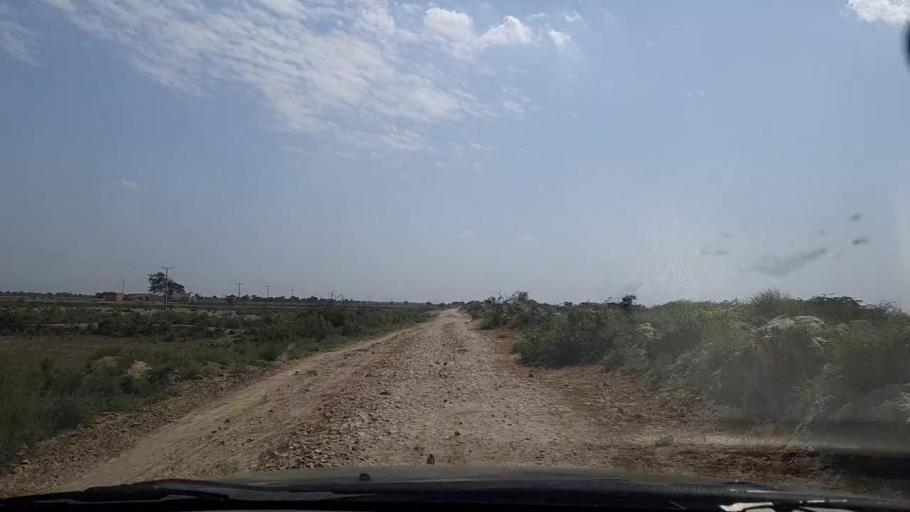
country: PK
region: Sindh
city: Mirpur Batoro
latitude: 24.5893
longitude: 68.1976
